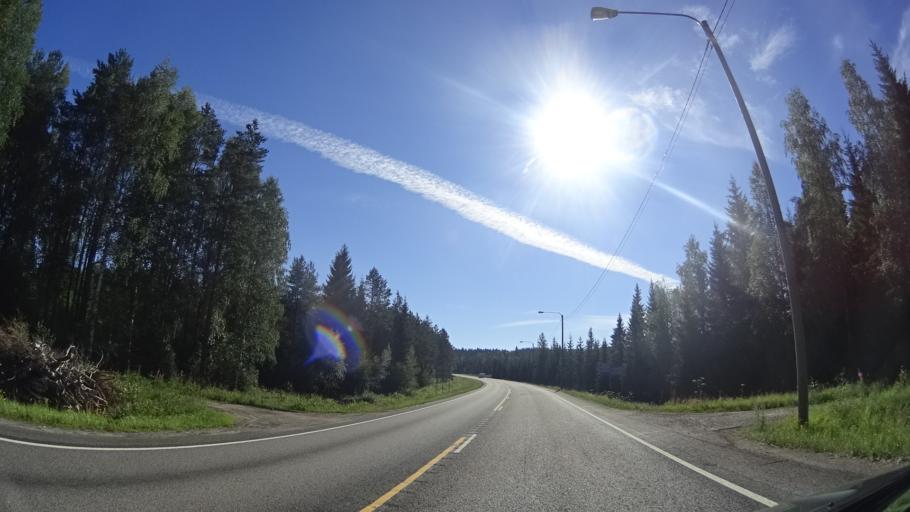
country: FI
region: Central Finland
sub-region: Jyvaeskylae
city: Petaejaevesi
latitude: 62.2704
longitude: 25.3327
